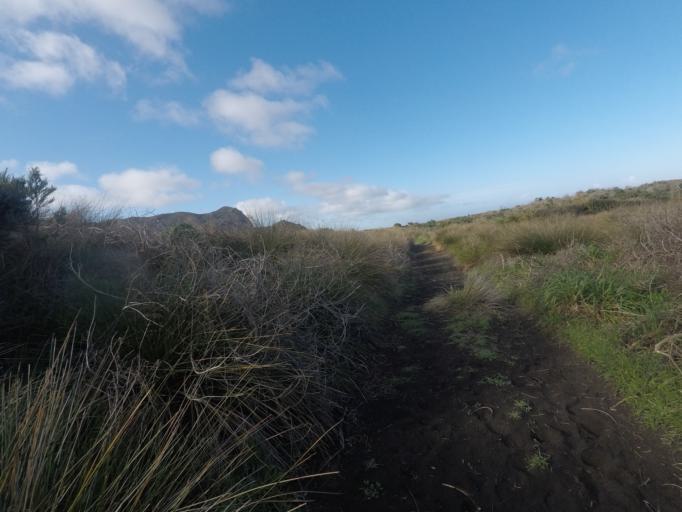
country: NZ
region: Auckland
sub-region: Auckland
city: Titirangi
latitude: -37.0051
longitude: 174.4796
